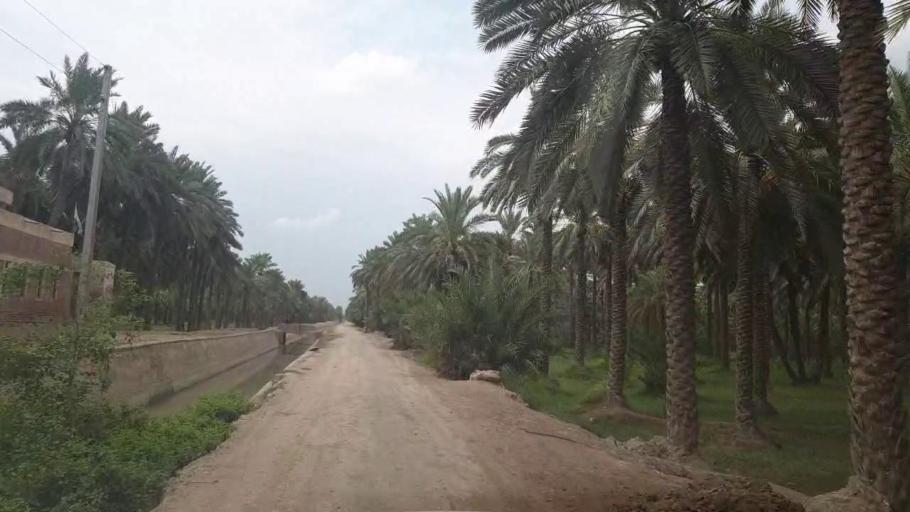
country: PK
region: Sindh
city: Sukkur
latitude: 27.6248
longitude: 68.8075
